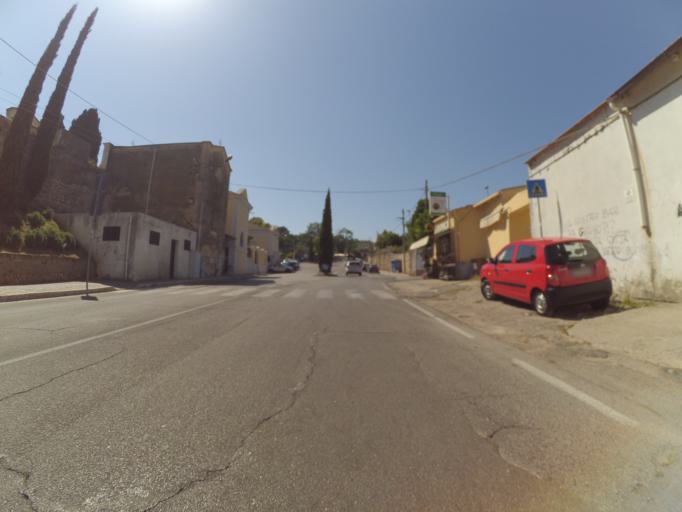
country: IT
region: Latium
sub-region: Provincia di Latina
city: Gaeta
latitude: 41.2158
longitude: 13.5615
